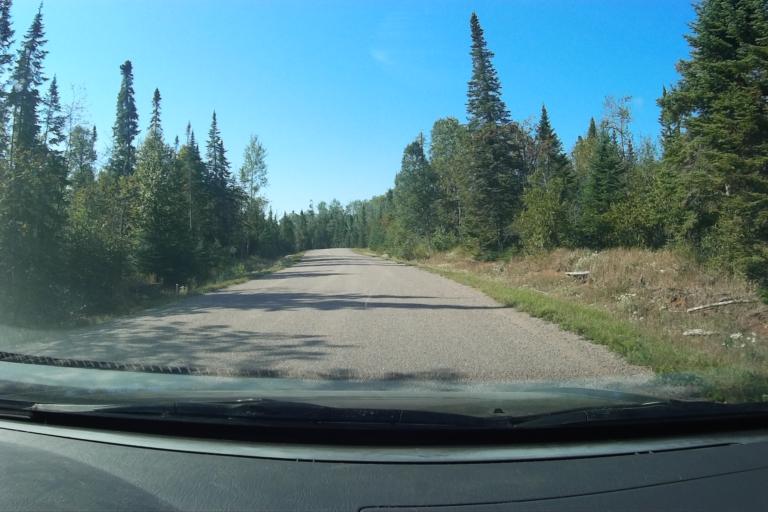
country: CA
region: Ontario
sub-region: Thunder Bay District
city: Thunder Bay
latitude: 48.3538
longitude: -88.8044
